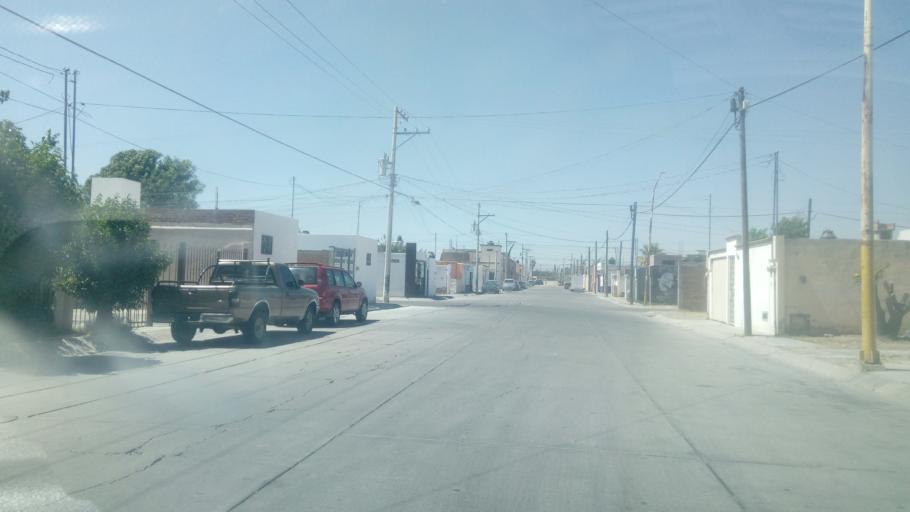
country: MX
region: Durango
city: Victoria de Durango
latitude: 24.0035
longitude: -104.6284
